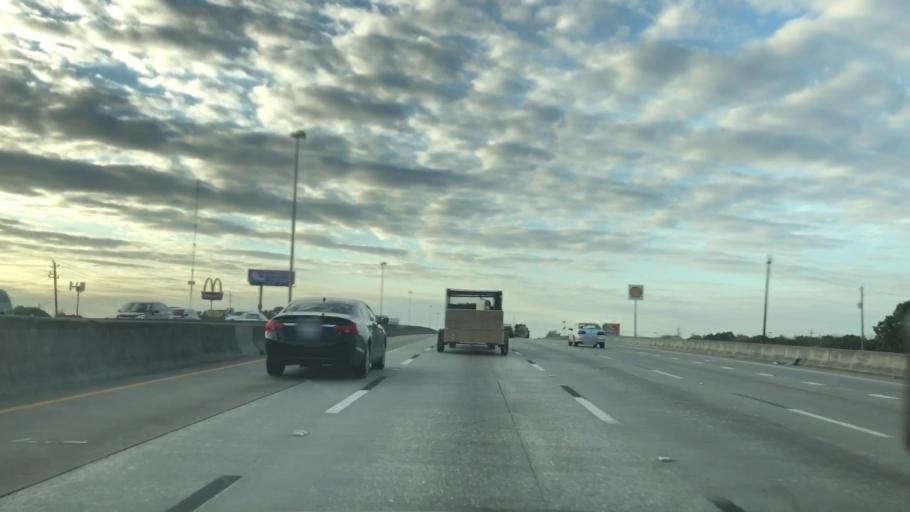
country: US
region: Texas
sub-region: Harris County
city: Aldine
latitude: 29.9163
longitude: -95.4127
